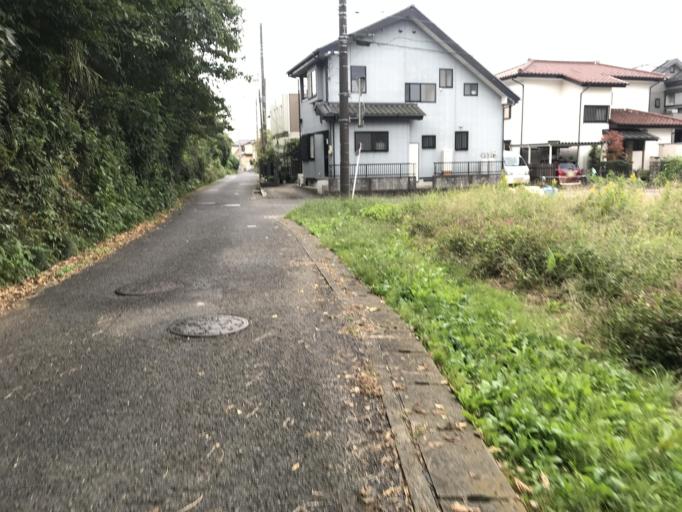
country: JP
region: Saitama
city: Shiraoka
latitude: 36.0097
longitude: 139.6562
